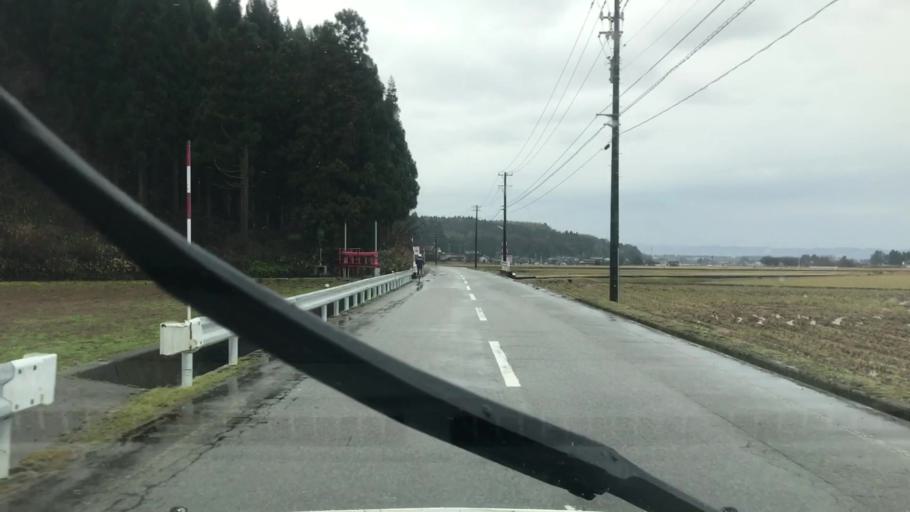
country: JP
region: Toyama
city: Toyama-shi
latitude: 36.6040
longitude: 137.2789
